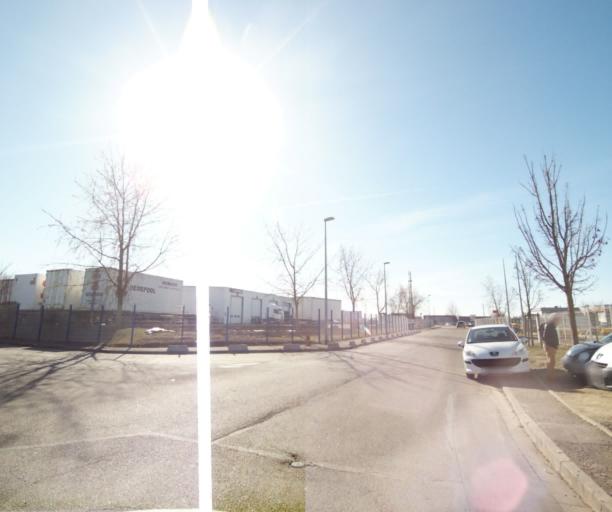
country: FR
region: Lorraine
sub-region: Departement de Meurthe-et-Moselle
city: Ludres
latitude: 48.6234
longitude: 6.1798
